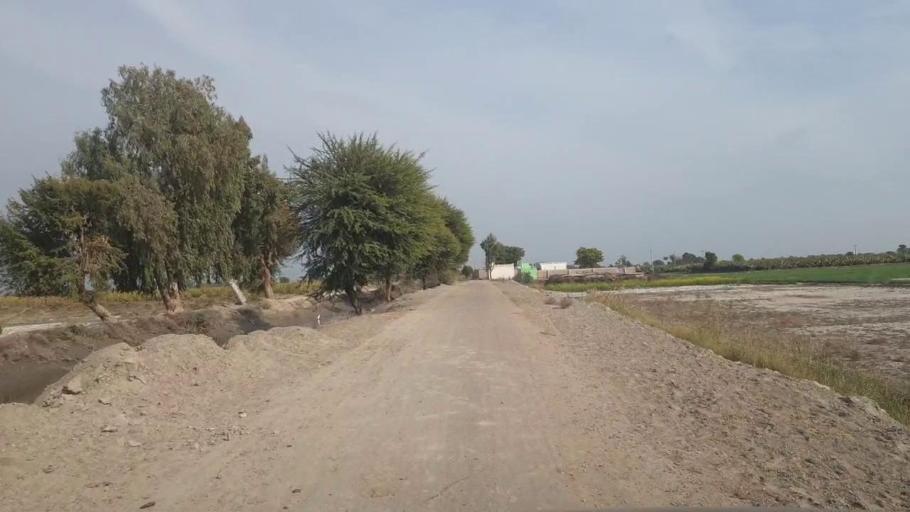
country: PK
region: Sindh
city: Shahpur Chakar
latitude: 26.0867
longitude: 68.4877
